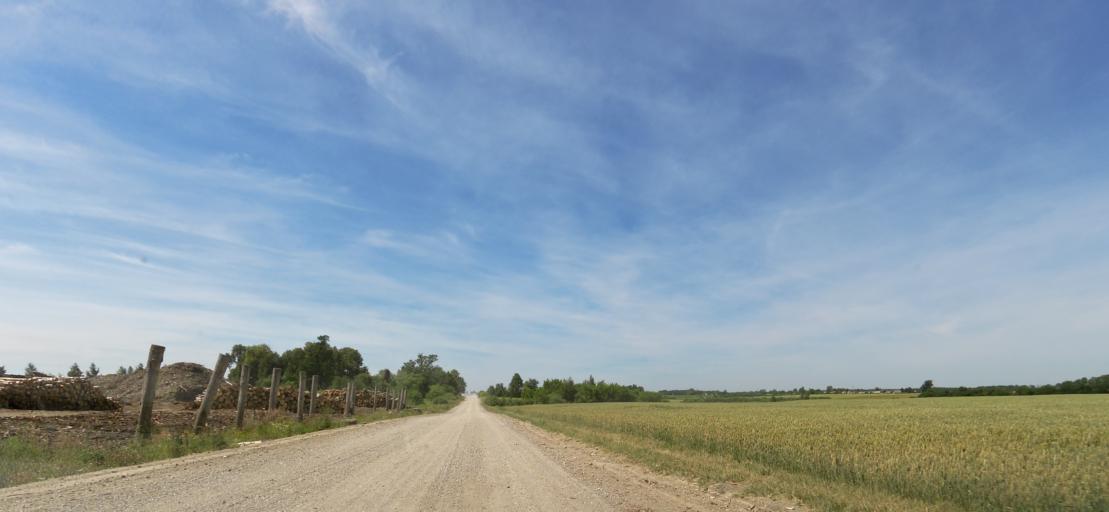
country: LT
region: Vilnius County
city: Ukmerge
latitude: 55.3021
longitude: 24.8078
